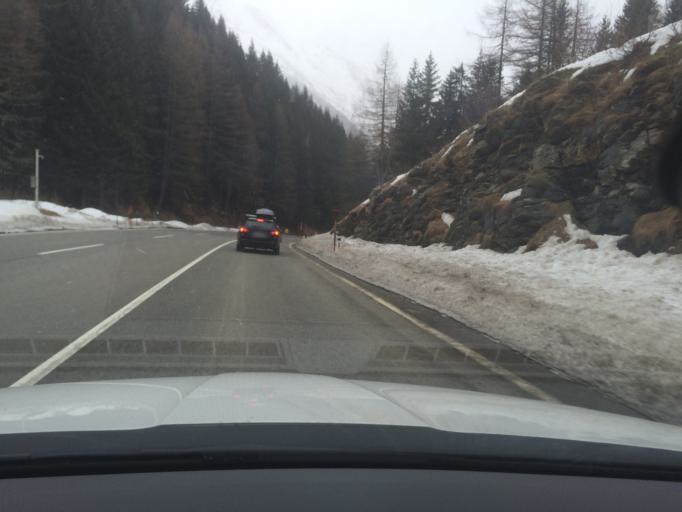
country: AT
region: Tyrol
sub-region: Politischer Bezirk Lienz
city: Matrei in Osttirol
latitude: 47.0968
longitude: 12.5169
